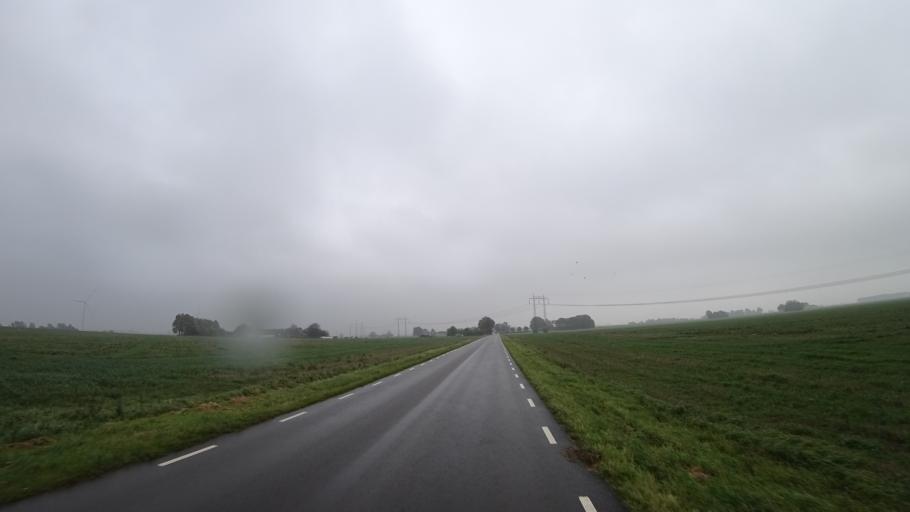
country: SE
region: Skane
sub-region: Kavlinge Kommun
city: Kaevlinge
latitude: 55.8199
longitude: 13.1179
